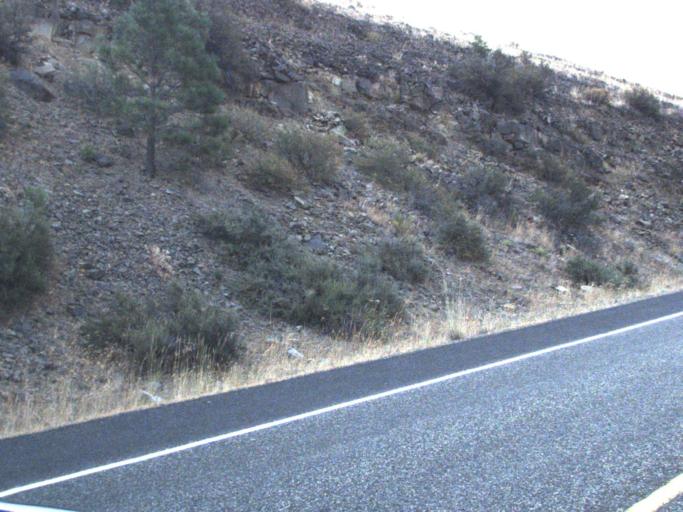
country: US
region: Washington
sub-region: Kittitas County
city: Ellensburg
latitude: 47.1703
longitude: -120.7031
